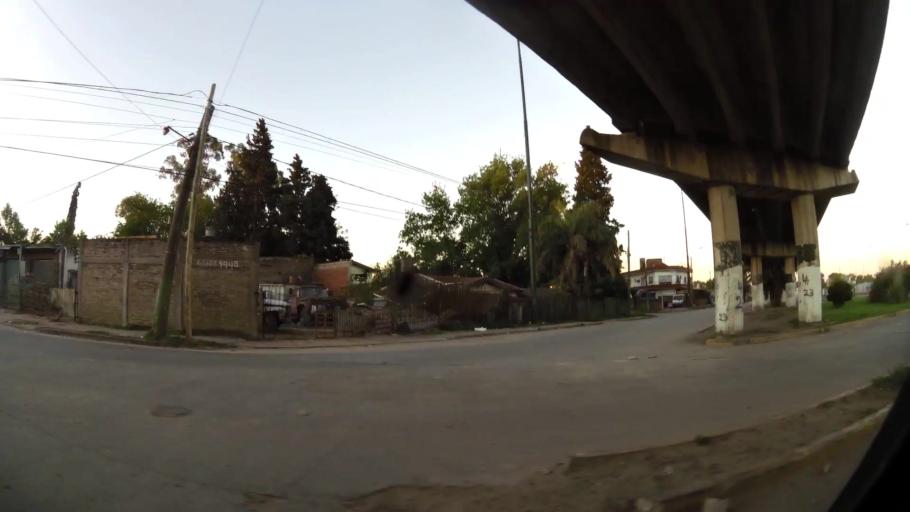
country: AR
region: Buenos Aires
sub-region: Partido de Almirante Brown
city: Adrogue
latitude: -34.8022
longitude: -58.3310
